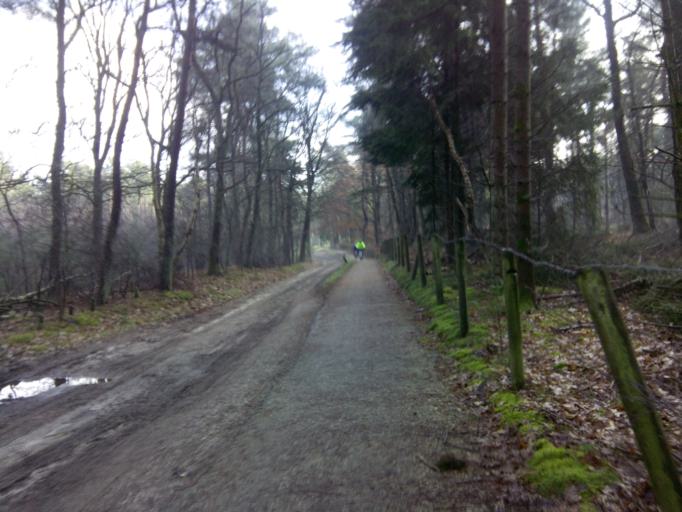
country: NL
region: Utrecht
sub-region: Gemeente Utrechtse Heuvelrug
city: Leersum
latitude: 52.0228
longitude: 5.4339
